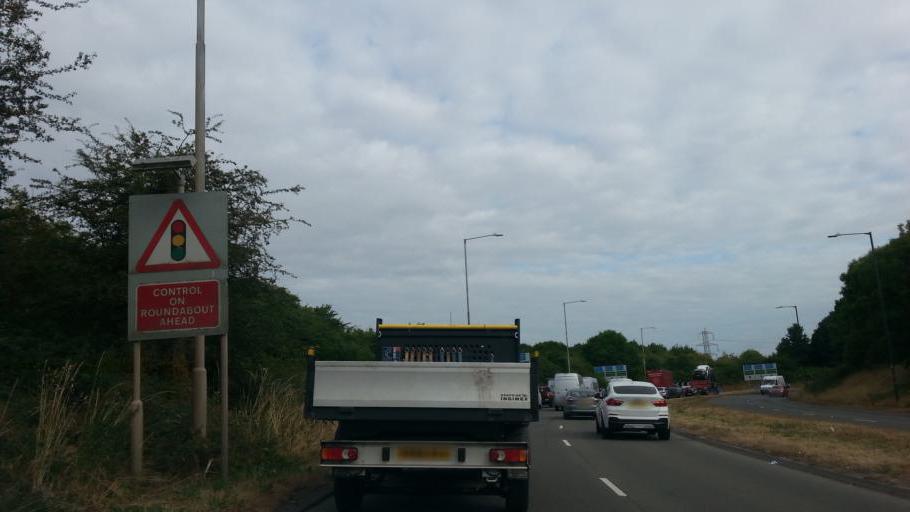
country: GB
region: England
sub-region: Warwickshire
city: Exhall
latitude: 52.4604
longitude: -1.4927
